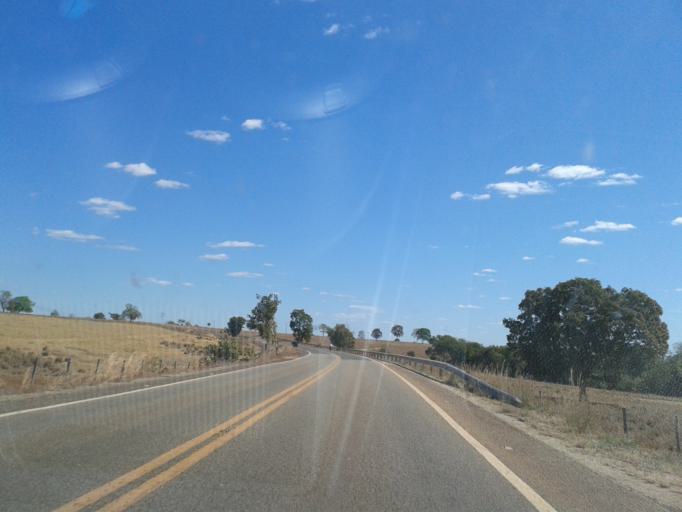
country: BR
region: Goias
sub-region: Sao Miguel Do Araguaia
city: Sao Miguel do Araguaia
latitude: -13.4001
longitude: -50.2565
